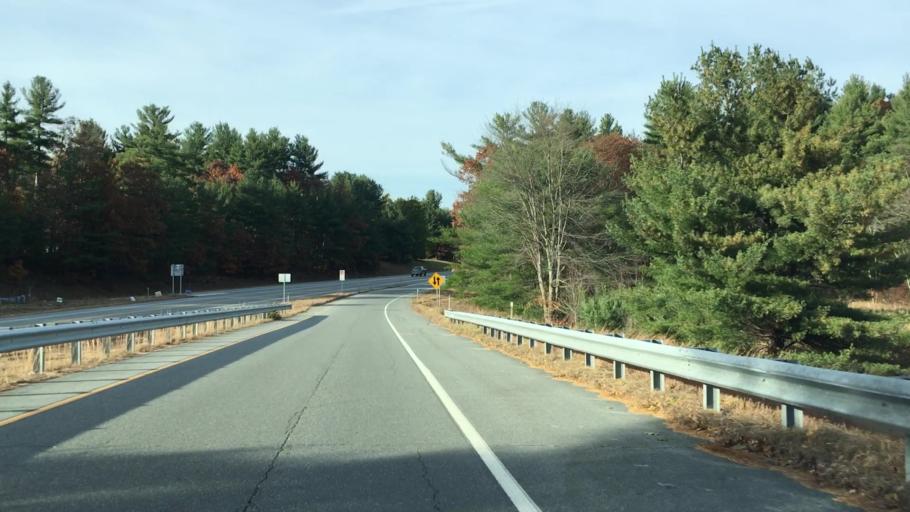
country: US
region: New Hampshire
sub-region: Hillsborough County
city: Milford
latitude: 42.8670
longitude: -71.6132
